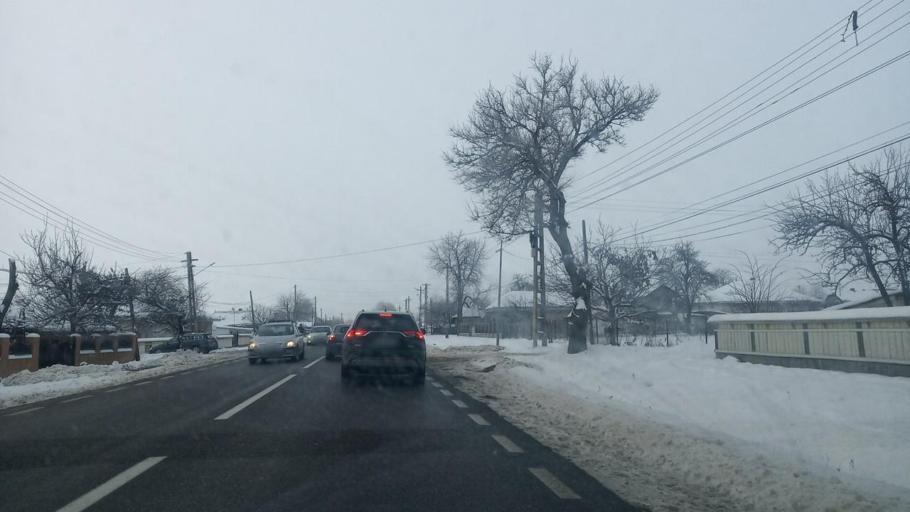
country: RO
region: Neamt
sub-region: Comuna Botesti
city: Nisiporesti
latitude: 47.0762
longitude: 26.7332
